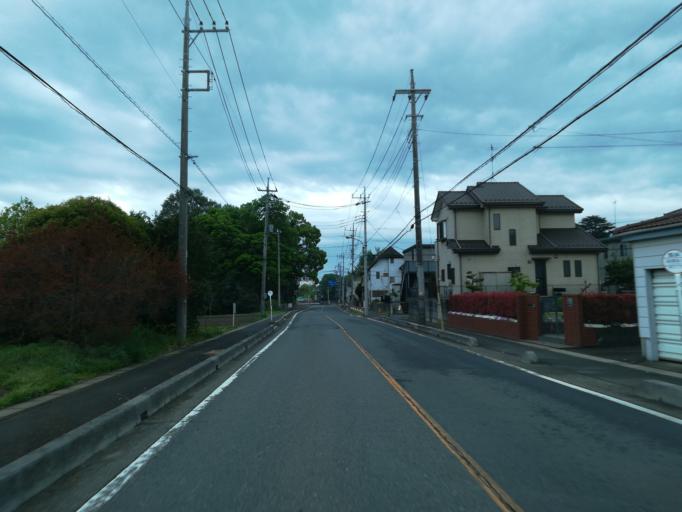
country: JP
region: Saitama
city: Hasuda
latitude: 35.9843
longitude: 139.6692
